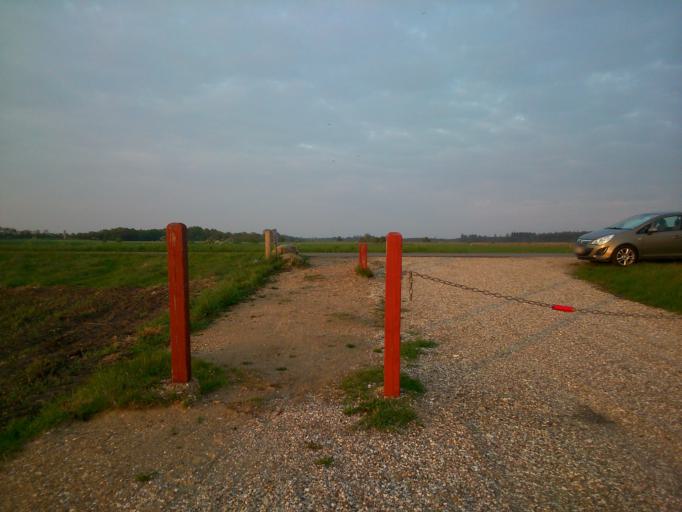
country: DK
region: Central Jutland
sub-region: Ringkobing-Skjern Kommune
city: Tarm
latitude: 55.9438
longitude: 8.6290
